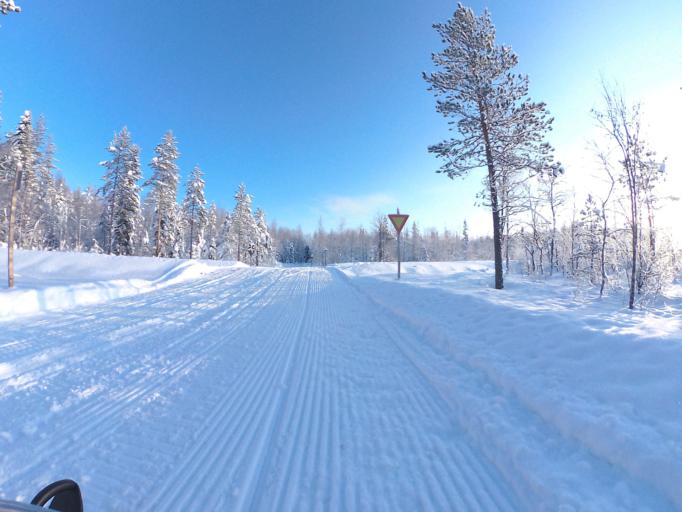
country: FI
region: Lapland
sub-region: Rovaniemi
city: Rovaniemi
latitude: 66.5973
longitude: 25.8462
